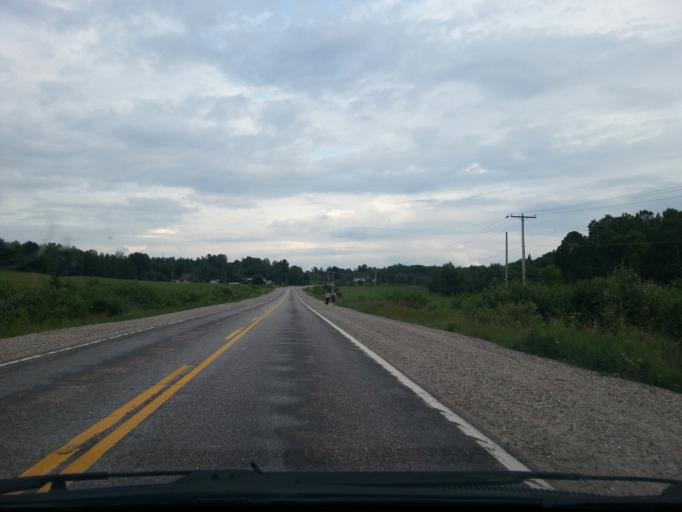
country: CA
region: Quebec
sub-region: Outaouais
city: Maniwaki
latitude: 46.1023
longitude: -76.0990
